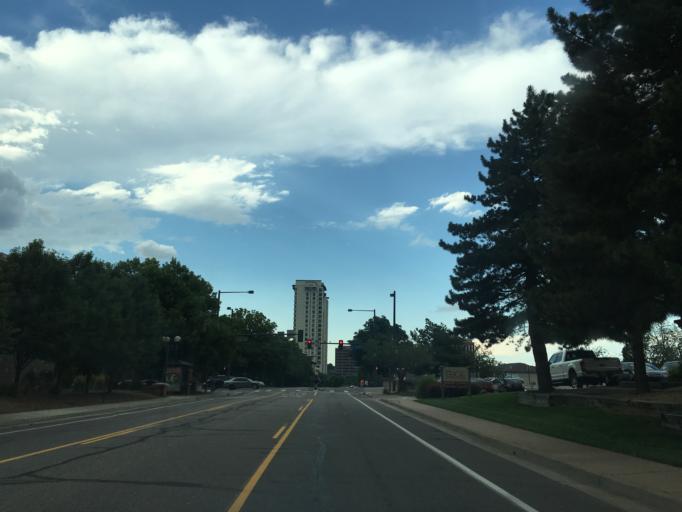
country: US
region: Colorado
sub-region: Arapahoe County
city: Glendale
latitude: 39.6995
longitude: -104.9340
